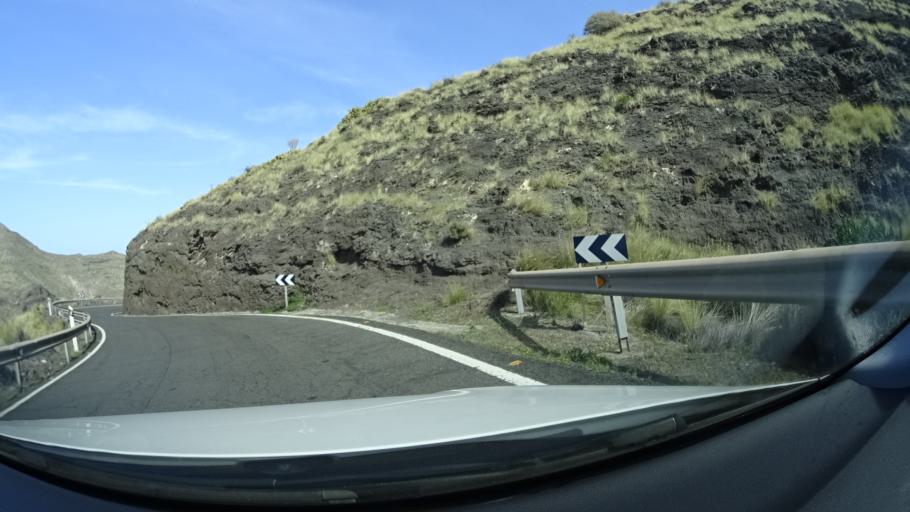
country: ES
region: Canary Islands
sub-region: Provincia de Las Palmas
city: Agaete
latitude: 28.0421
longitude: -15.7349
